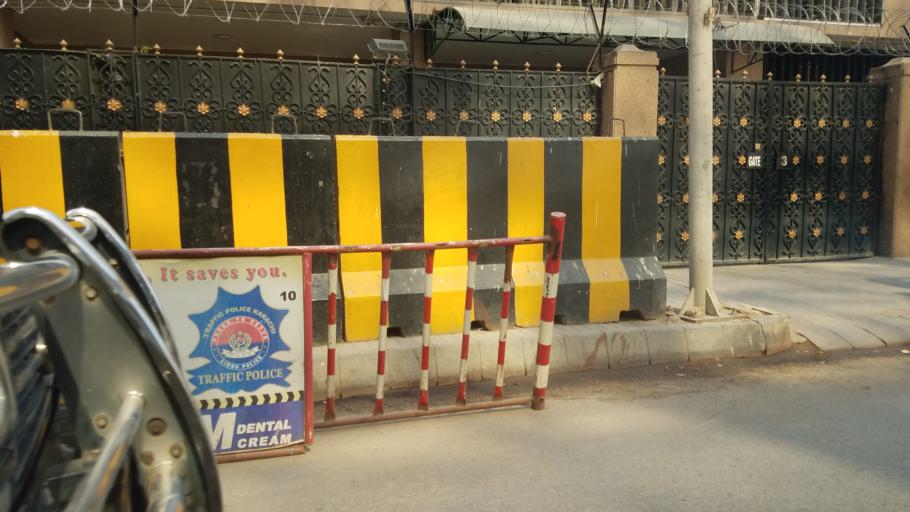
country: PK
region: Sindh
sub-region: Karachi District
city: Karachi
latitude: 24.8489
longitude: 67.0026
